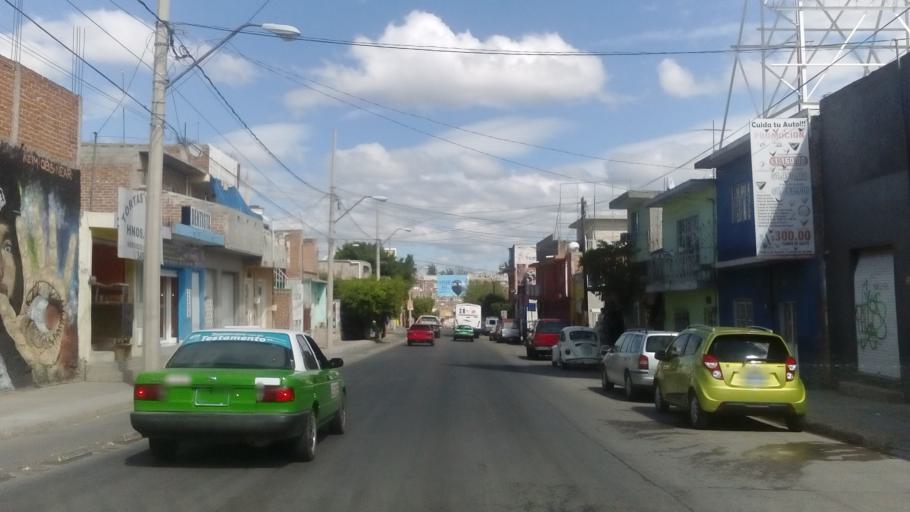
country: MX
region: Guanajuato
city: Leon
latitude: 21.1396
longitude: -101.7017
